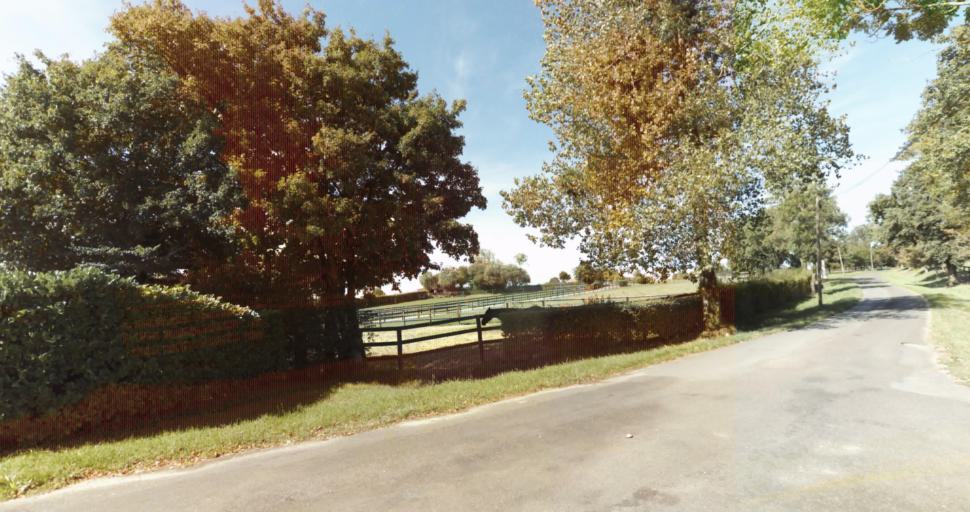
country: FR
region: Lower Normandy
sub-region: Departement de l'Orne
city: Gace
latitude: 48.7569
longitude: 0.2362
